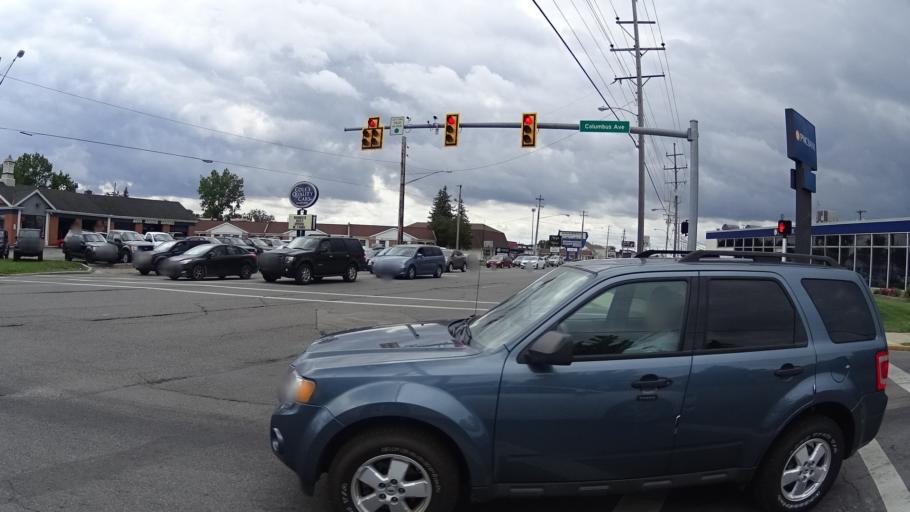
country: US
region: Ohio
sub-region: Erie County
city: Sandusky
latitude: 41.4330
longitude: -82.6980
